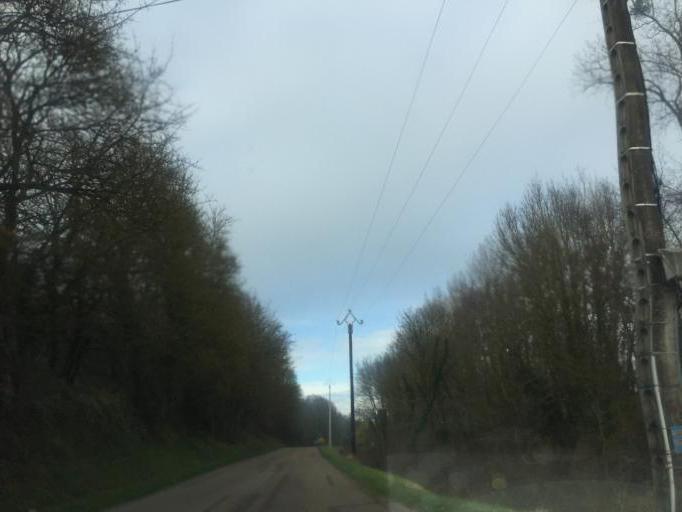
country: FR
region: Bourgogne
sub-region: Departement de la Nievre
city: Clamecy
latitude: 47.5027
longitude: 3.5132
